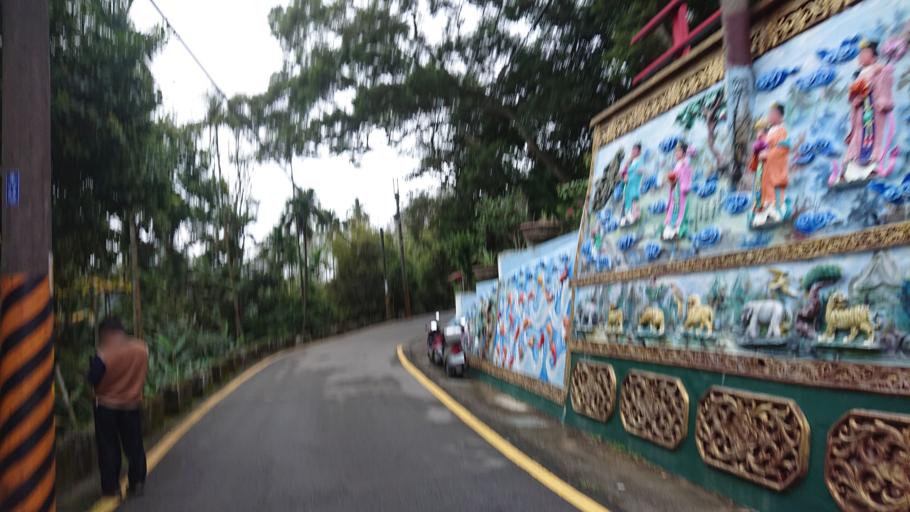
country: TW
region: Taiwan
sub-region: Taoyuan
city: Taoyuan
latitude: 24.9309
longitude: 121.3617
